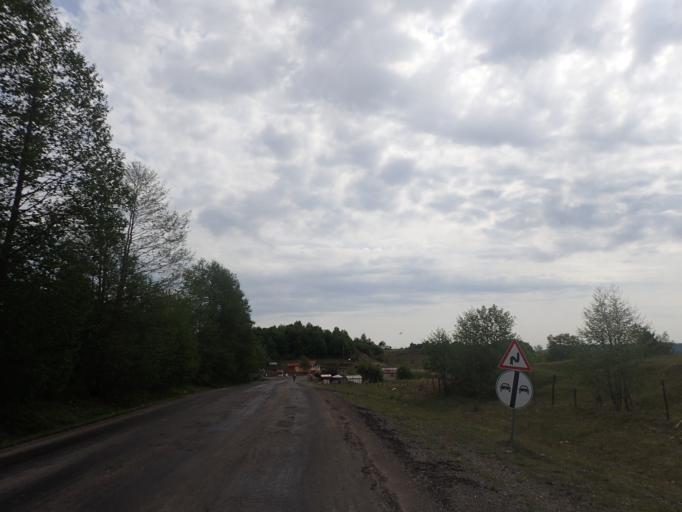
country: TR
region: Ordu
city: Akkus
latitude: 40.8754
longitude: 37.0413
